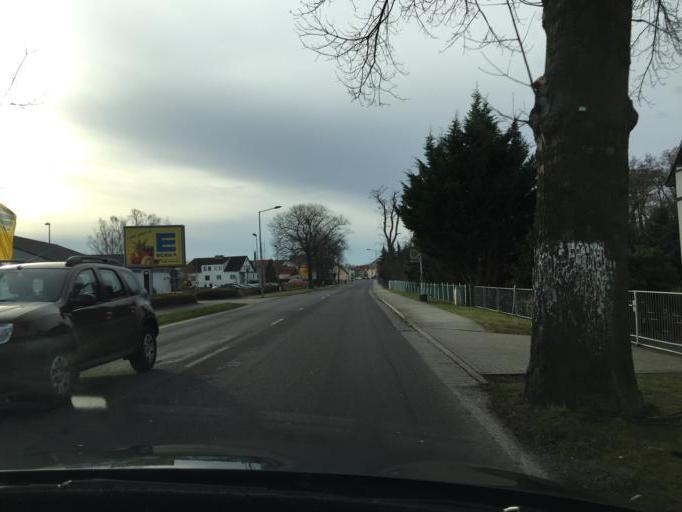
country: DE
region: Brandenburg
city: Peitz
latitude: 51.8612
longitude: 14.4144
